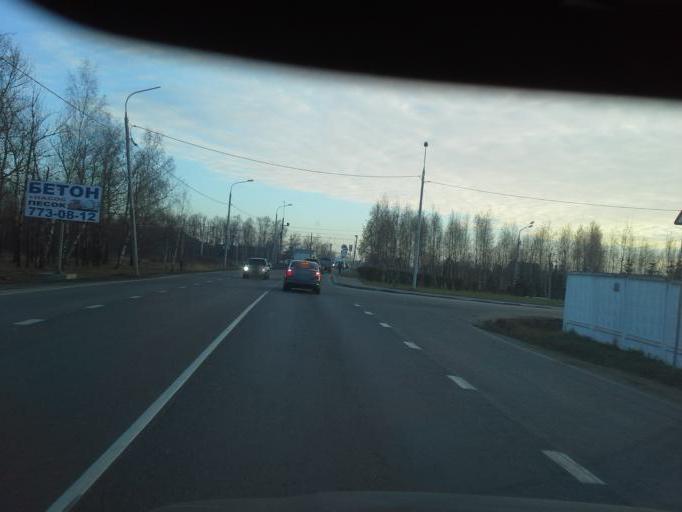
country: RU
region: Moskovskaya
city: Kokoshkino
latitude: 55.5844
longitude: 37.1227
